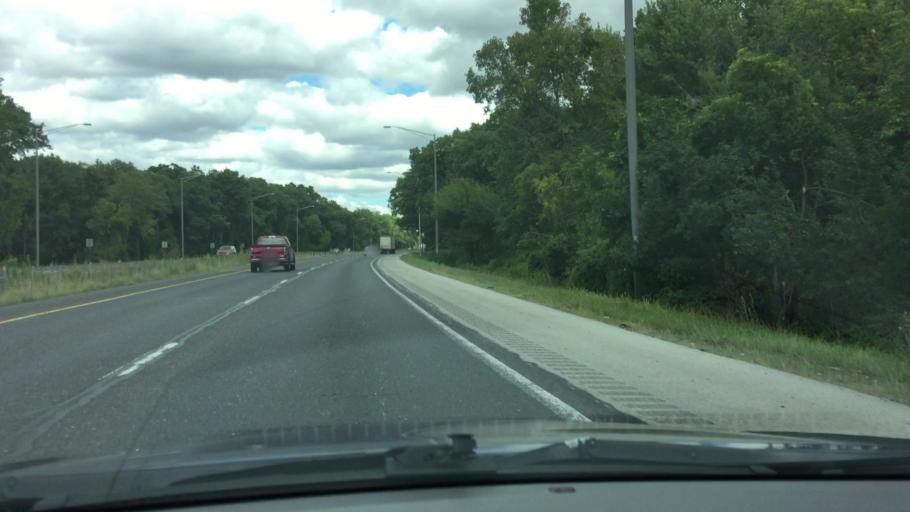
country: US
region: Illinois
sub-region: Cook County
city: Glenwood
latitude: 41.5508
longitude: -87.5831
